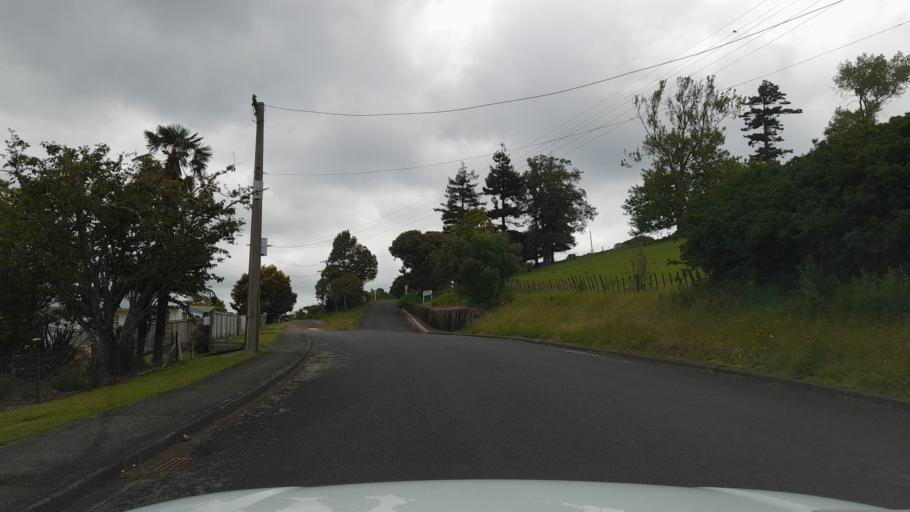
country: NZ
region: Northland
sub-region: Far North District
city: Waimate North
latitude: -35.4094
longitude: 173.7873
